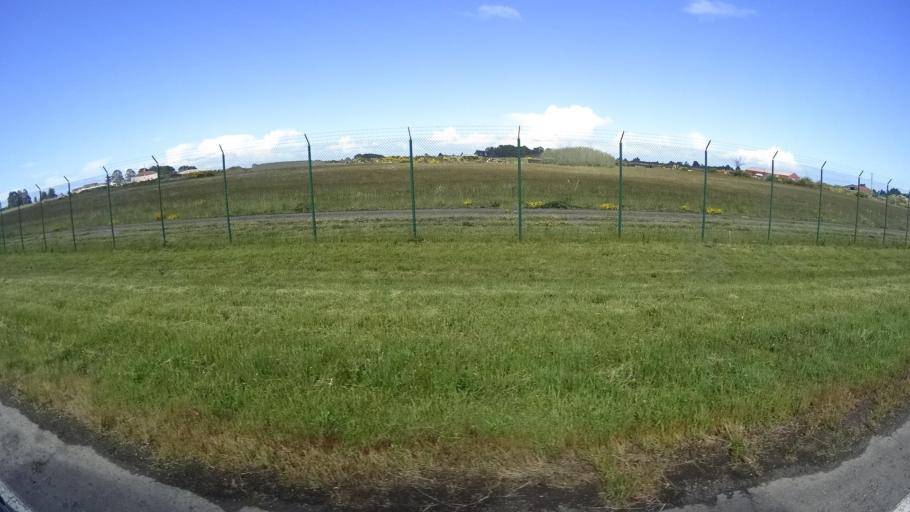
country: US
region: California
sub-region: Humboldt County
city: McKinleyville
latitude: 40.9763
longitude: -124.1006
